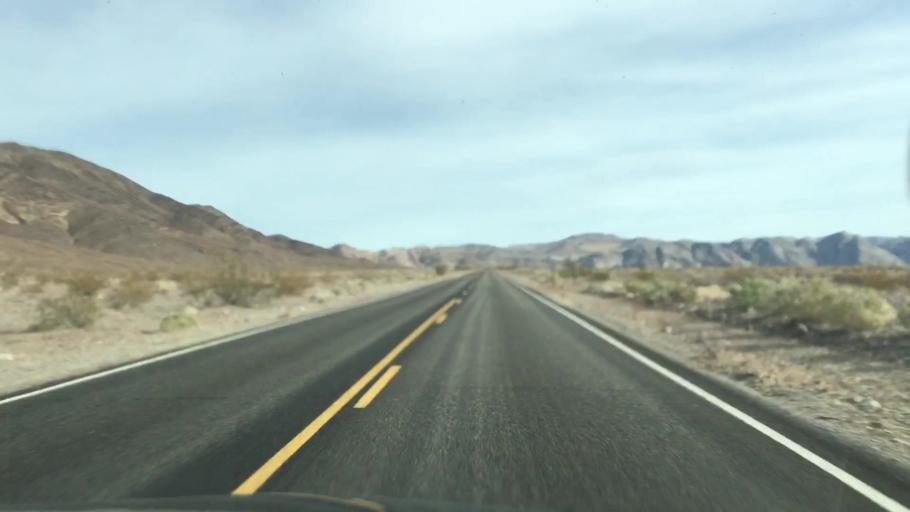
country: US
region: Nevada
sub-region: Nye County
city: Beatty
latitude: 36.7037
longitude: -116.9957
